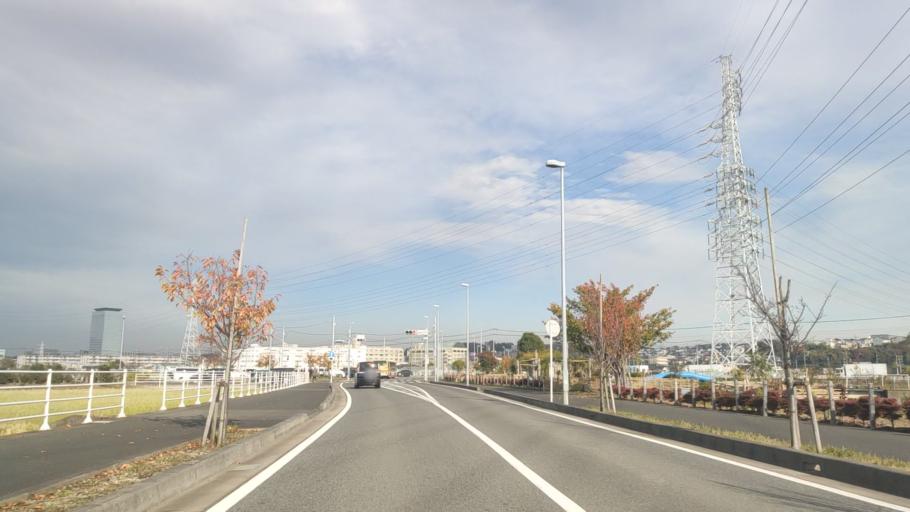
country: JP
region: Kanagawa
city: Atsugi
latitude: 35.4383
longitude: 139.3886
